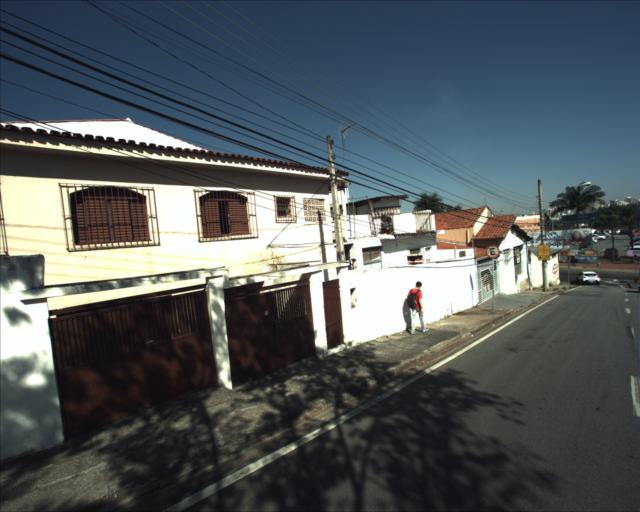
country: BR
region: Sao Paulo
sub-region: Sorocaba
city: Sorocaba
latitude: -23.4953
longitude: -47.4414
